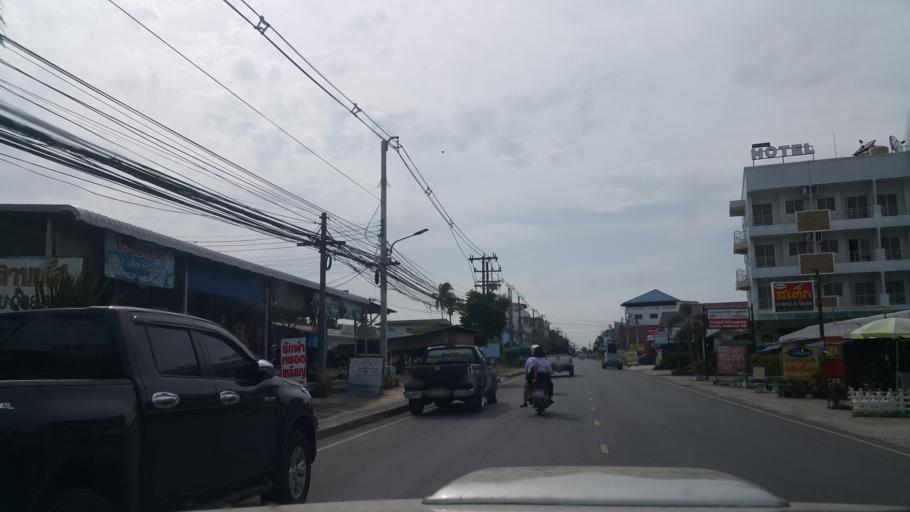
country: TH
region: Rayong
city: Ban Chang
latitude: 12.7294
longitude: 101.0513
